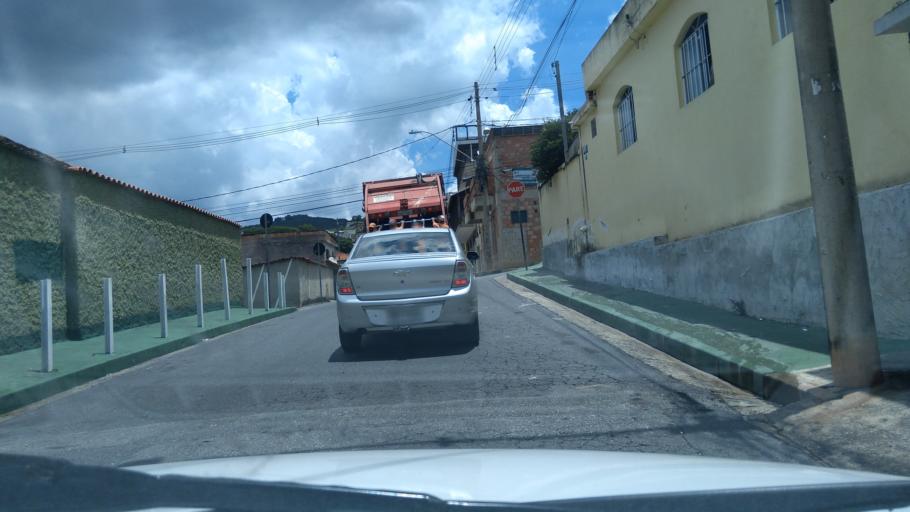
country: BR
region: Minas Gerais
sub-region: Belo Horizonte
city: Belo Horizonte
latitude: -19.9153
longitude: -43.8930
